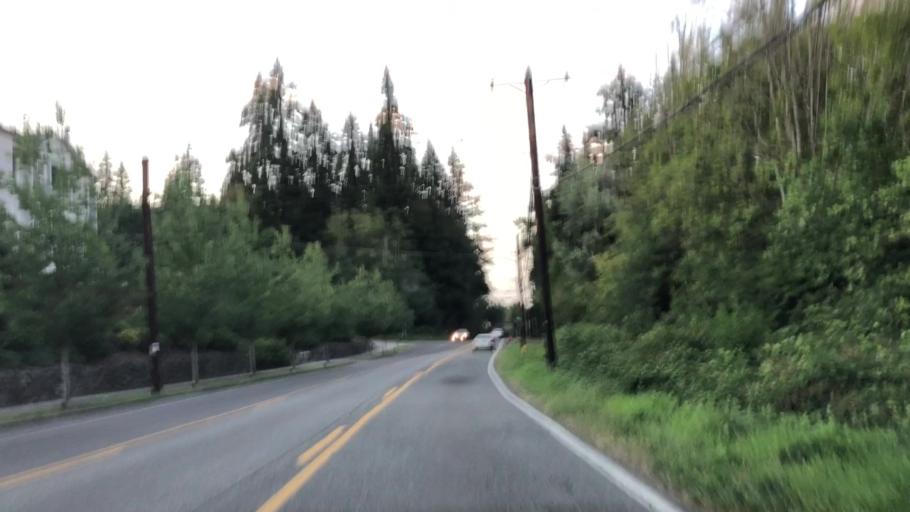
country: US
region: Washington
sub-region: Snohomish County
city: Martha Lake
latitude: 47.8562
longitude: -122.2717
